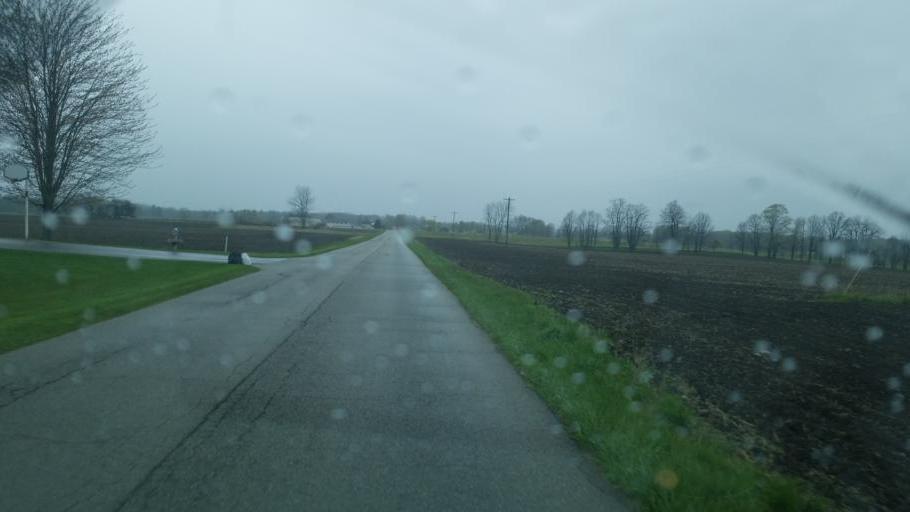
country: US
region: Michigan
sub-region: Montcalm County
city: Lakeview
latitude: 43.5110
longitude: -85.2959
